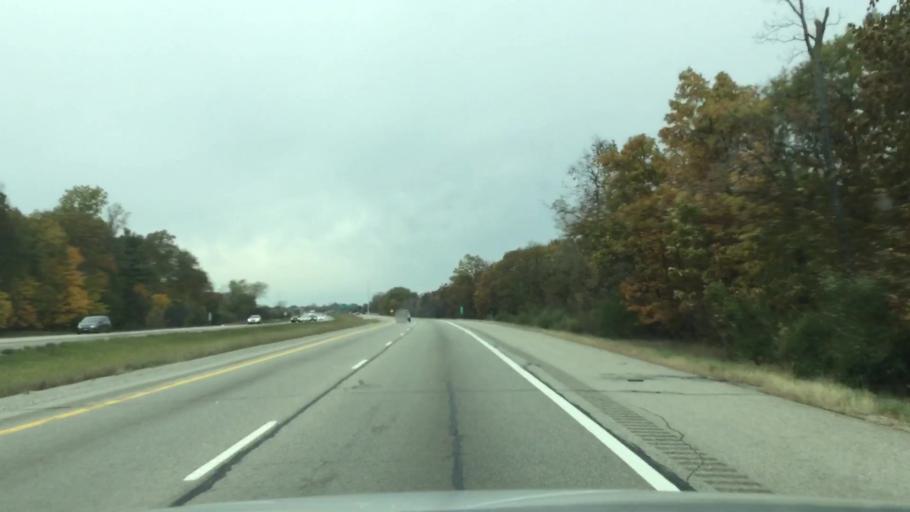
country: US
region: Michigan
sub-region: Washtenaw County
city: Ann Arbor
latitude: 42.3255
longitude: -83.6751
